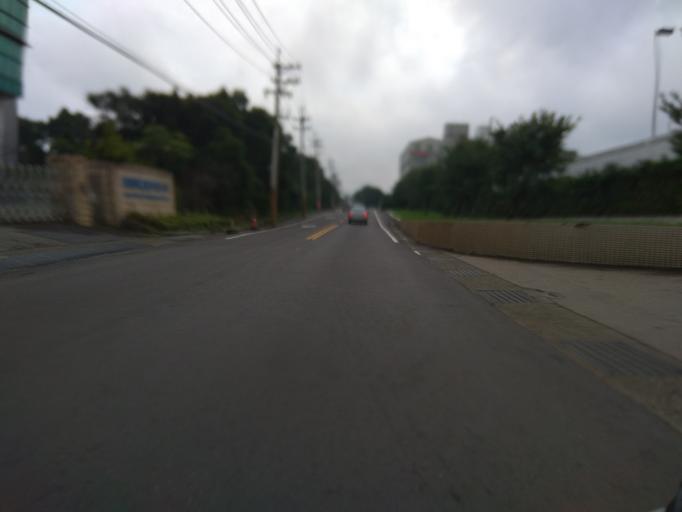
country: TW
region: Taiwan
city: Daxi
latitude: 24.9261
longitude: 121.1567
